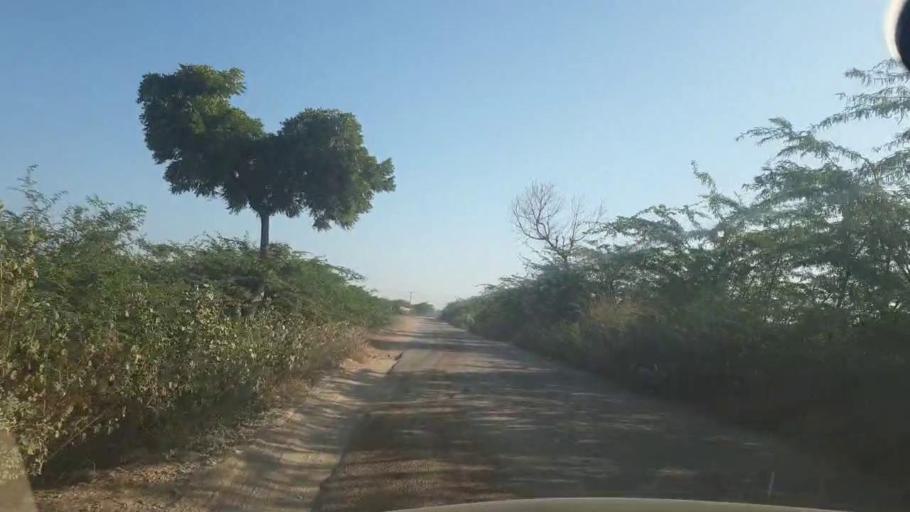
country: PK
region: Sindh
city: Malir Cantonment
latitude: 25.1095
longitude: 67.2648
